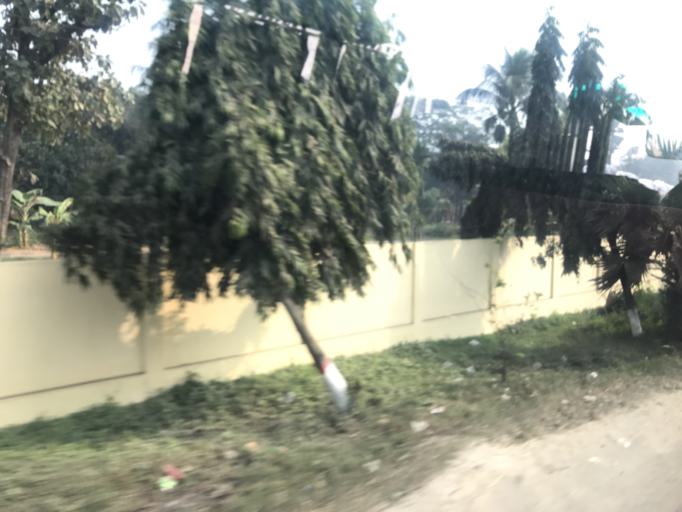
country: BD
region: Dhaka
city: Tungi
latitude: 23.9039
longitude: 90.2682
